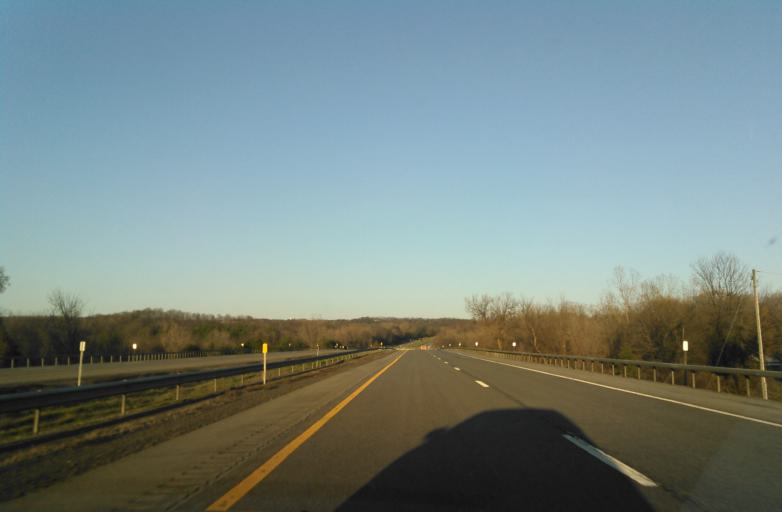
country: US
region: New York
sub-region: Ontario County
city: Victor
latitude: 43.0144
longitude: -77.4728
